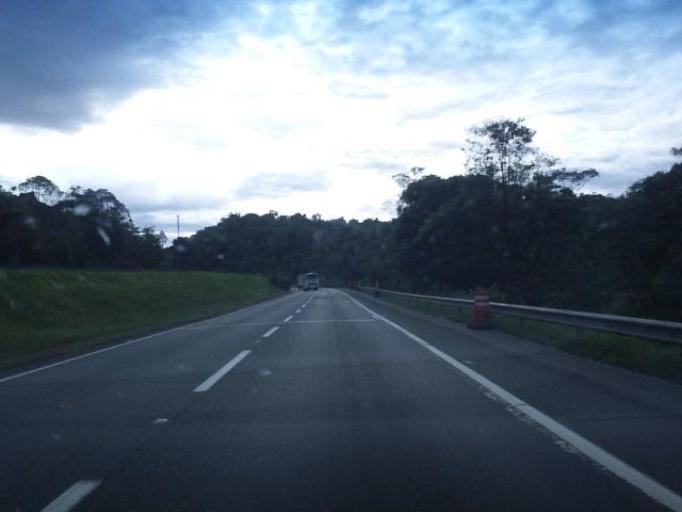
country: BR
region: Parana
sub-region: Antonina
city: Antonina
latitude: -25.0971
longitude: -48.6706
